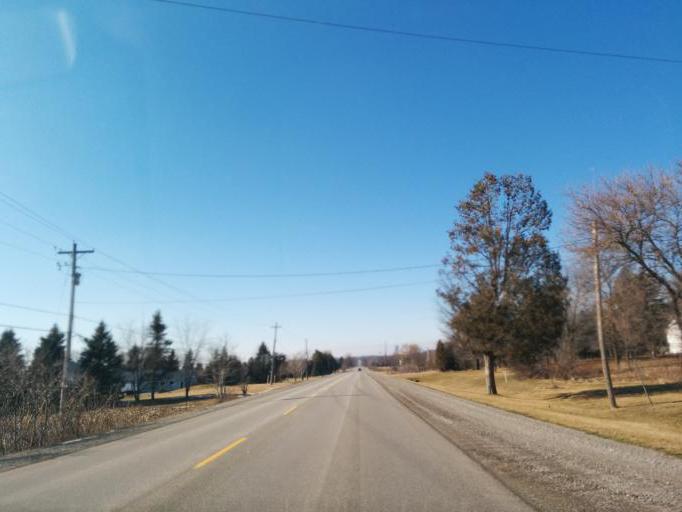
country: CA
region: Ontario
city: Brant
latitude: 43.0305
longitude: -80.3401
